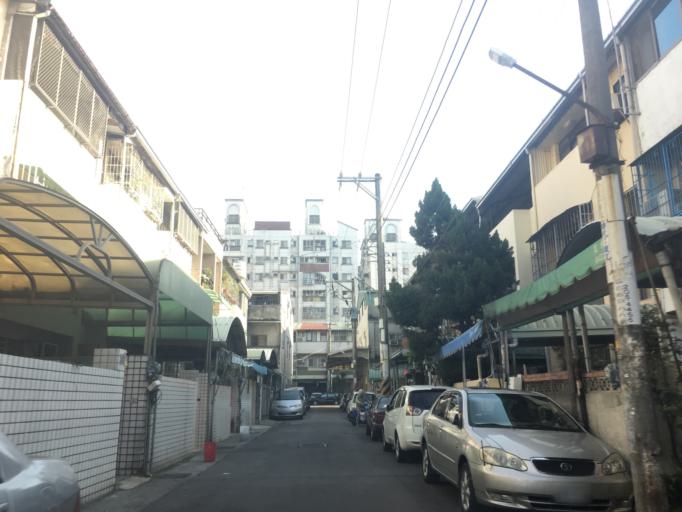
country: TW
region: Taiwan
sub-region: Taichung City
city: Taichung
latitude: 24.1796
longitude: 120.6912
